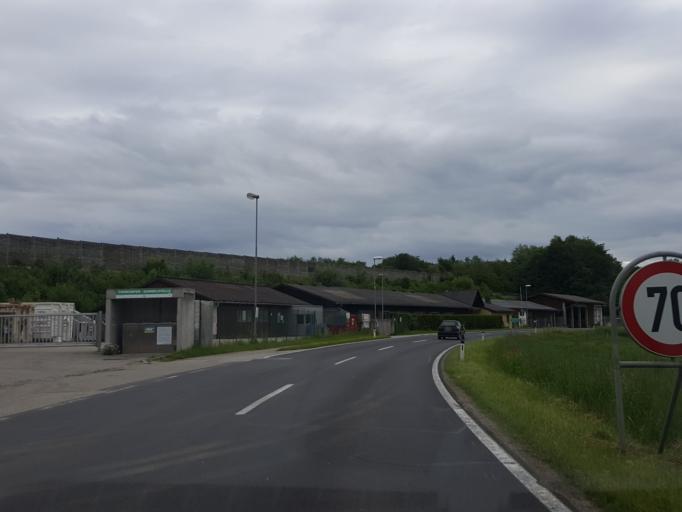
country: AT
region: Upper Austria
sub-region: Politischer Bezirk Vocklabruck
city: Seewalchen
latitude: 47.9557
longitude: 13.5935
